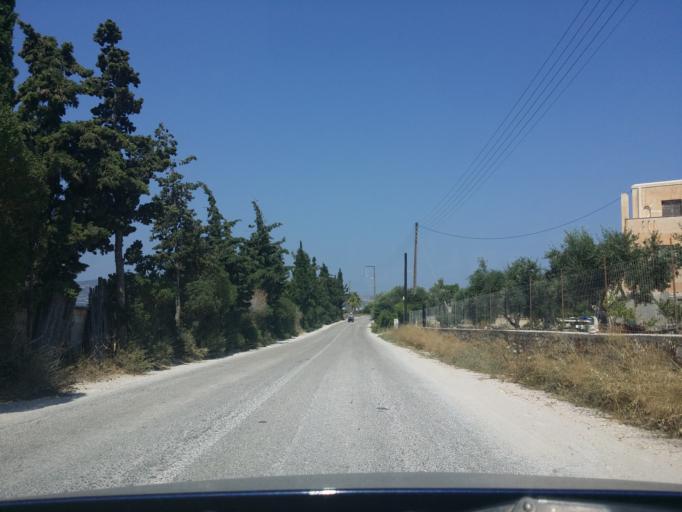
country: GR
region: South Aegean
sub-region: Nomos Kykladon
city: Antiparos
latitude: 37.0035
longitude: 25.1465
